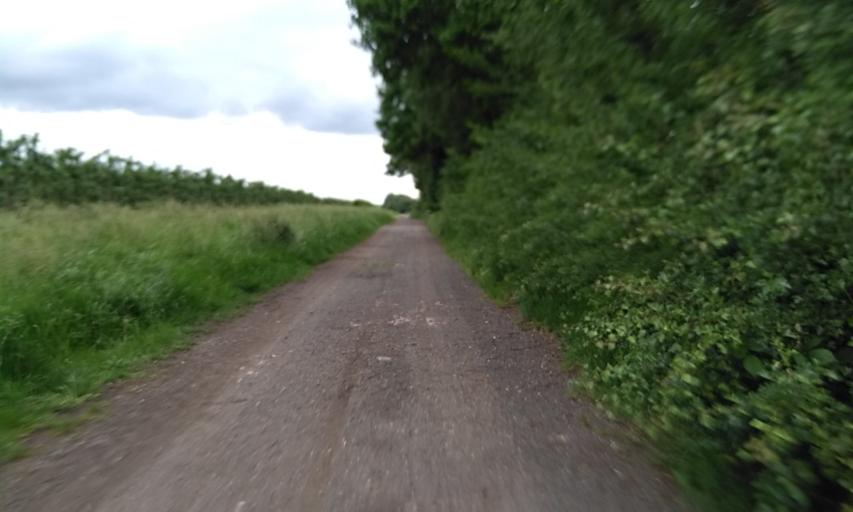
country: DE
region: Lower Saxony
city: Apensen
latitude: 53.4497
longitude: 9.6163
